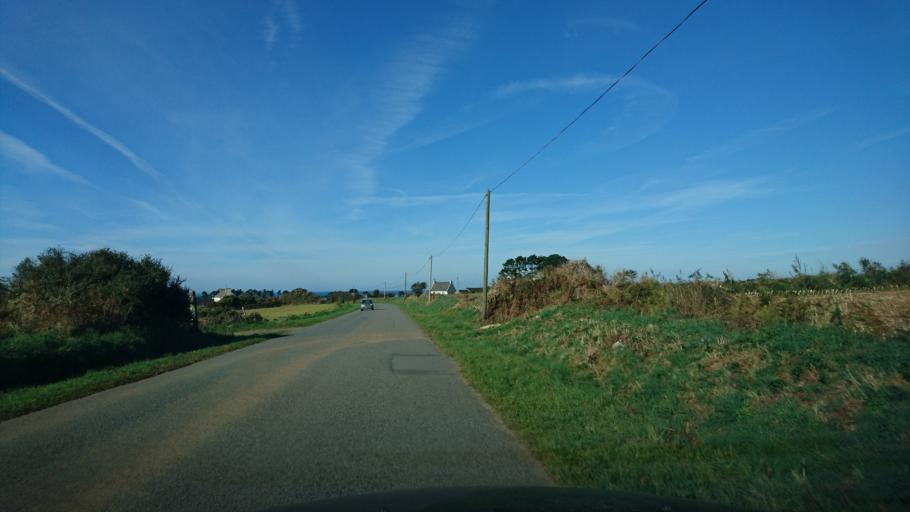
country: FR
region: Brittany
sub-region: Departement du Finistere
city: Lampaul-Plouarzel
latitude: 48.4289
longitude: -4.7560
